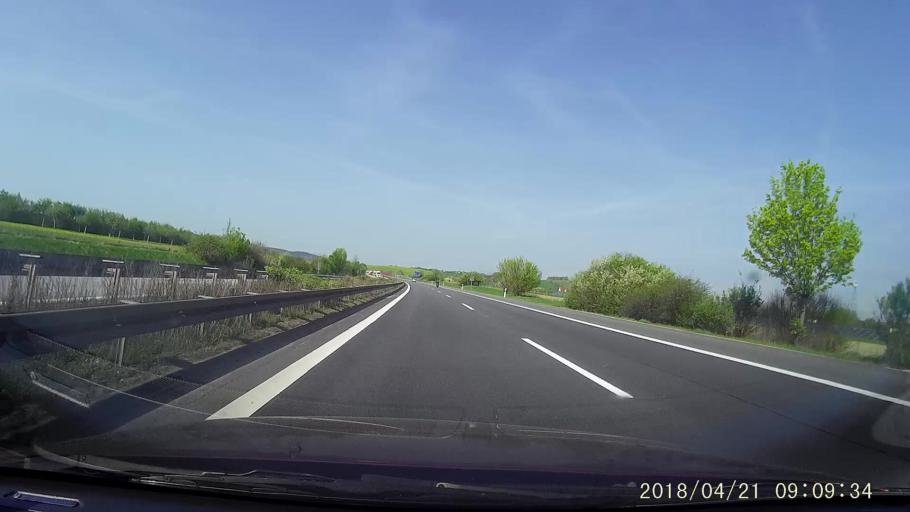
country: DE
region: Saxony
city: Kodersdorf
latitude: 51.2234
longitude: 14.9058
